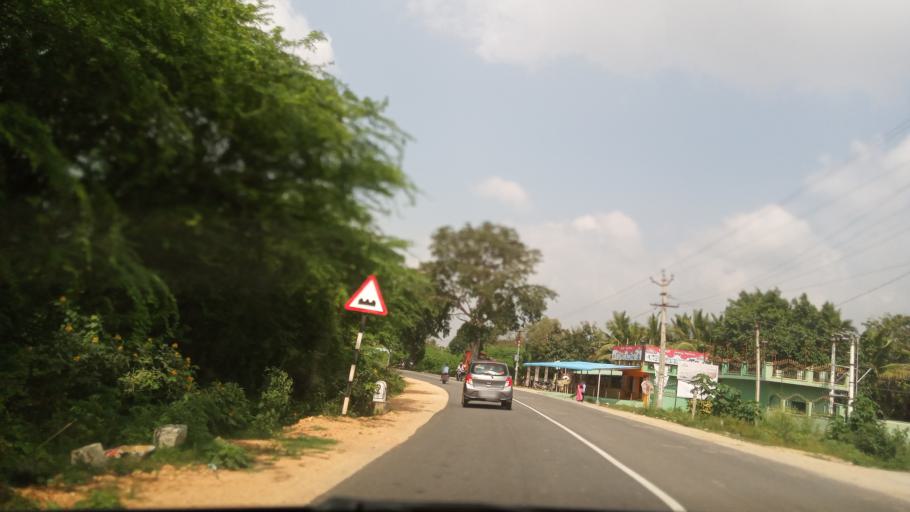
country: IN
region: Andhra Pradesh
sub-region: Chittoor
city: Madanapalle
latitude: 13.6335
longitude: 78.5549
